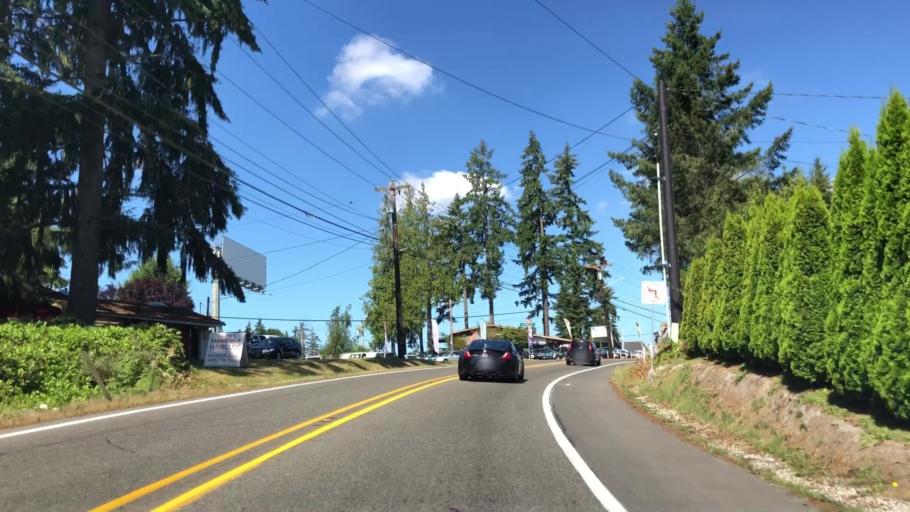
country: US
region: Washington
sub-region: Snohomish County
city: Alderwood Manor
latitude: 47.8197
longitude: -122.2592
